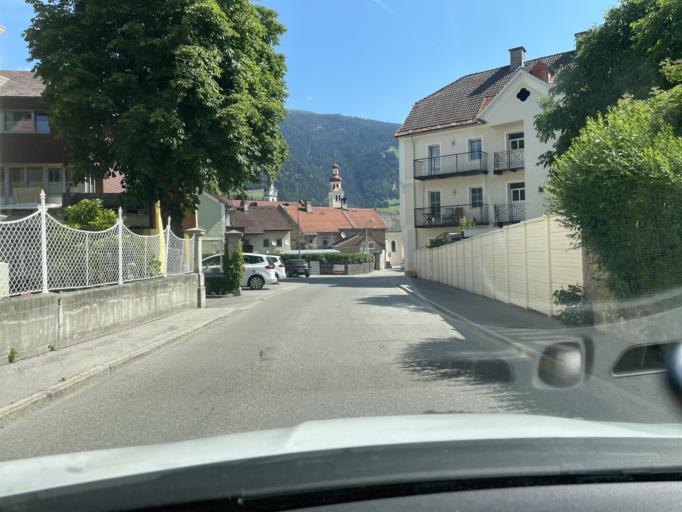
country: AT
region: Tyrol
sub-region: Politischer Bezirk Lienz
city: Lienz
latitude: 46.8308
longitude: 12.7591
